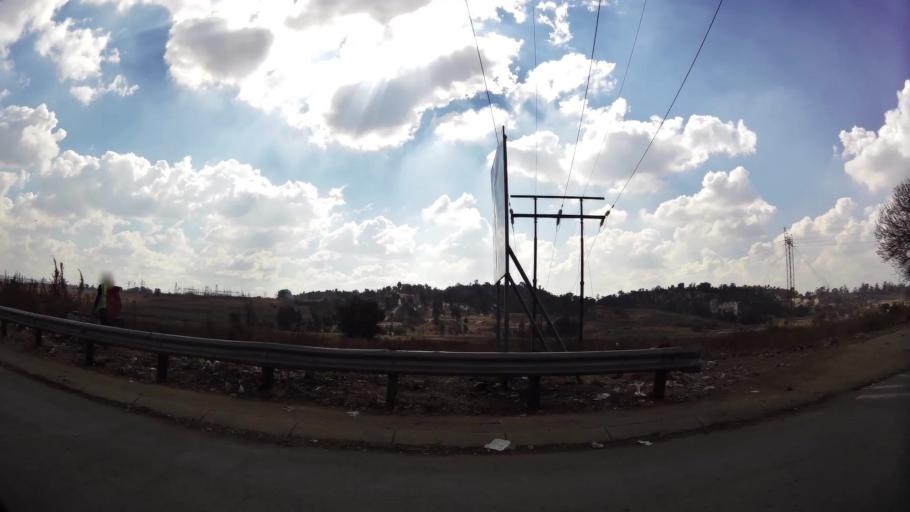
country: ZA
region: Gauteng
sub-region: City of Johannesburg Metropolitan Municipality
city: Roodepoort
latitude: -26.1817
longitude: 27.8517
